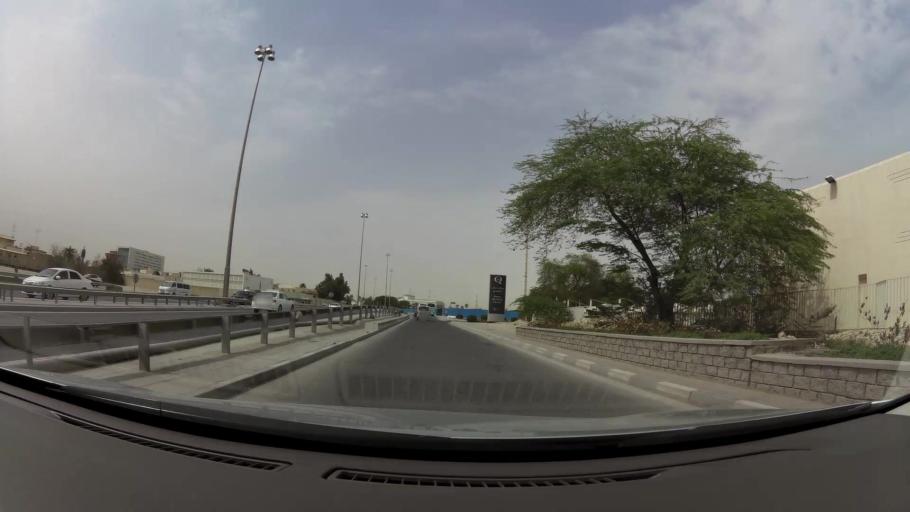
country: QA
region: Baladiyat ad Dawhah
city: Doha
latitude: 25.2916
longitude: 51.5155
